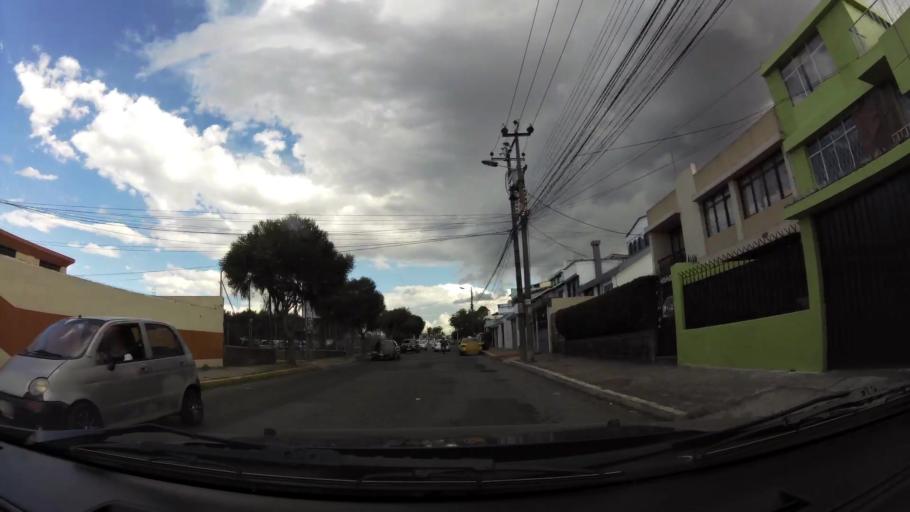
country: EC
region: Pichincha
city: Quito
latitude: -0.1238
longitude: -78.4917
